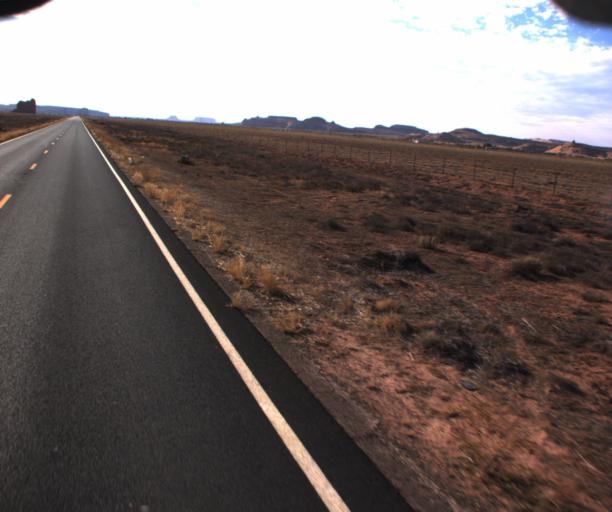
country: US
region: Arizona
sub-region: Apache County
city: Many Farms
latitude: 36.7592
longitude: -109.6490
